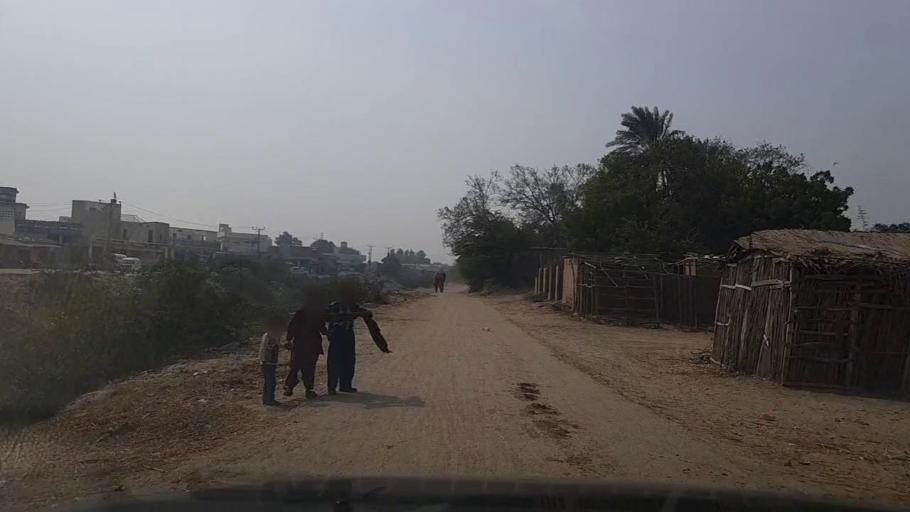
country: PK
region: Sindh
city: Thatta
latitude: 24.5530
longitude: 67.8422
